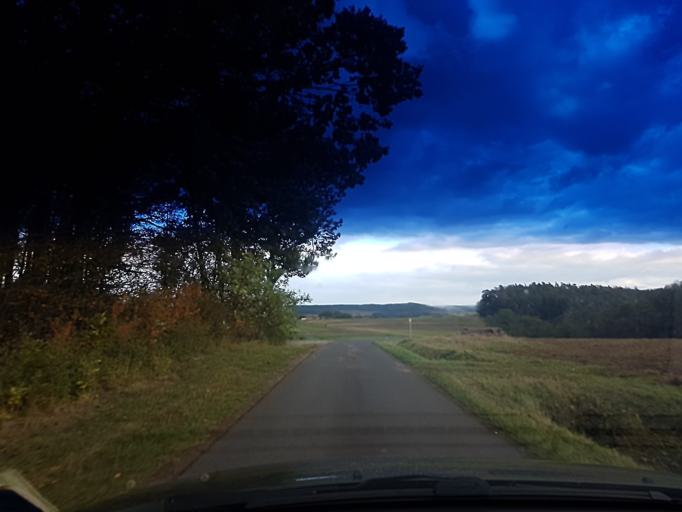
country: DE
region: Bavaria
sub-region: Regierungsbezirk Mittelfranken
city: Burghaslach
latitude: 49.7450
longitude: 10.5886
